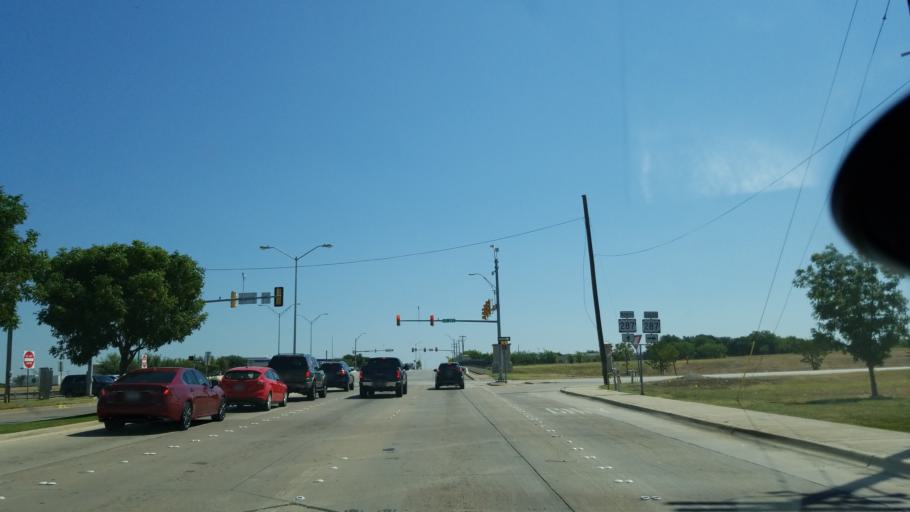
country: US
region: Texas
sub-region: Tarrant County
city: Mansfield
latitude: 32.5674
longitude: -97.1186
